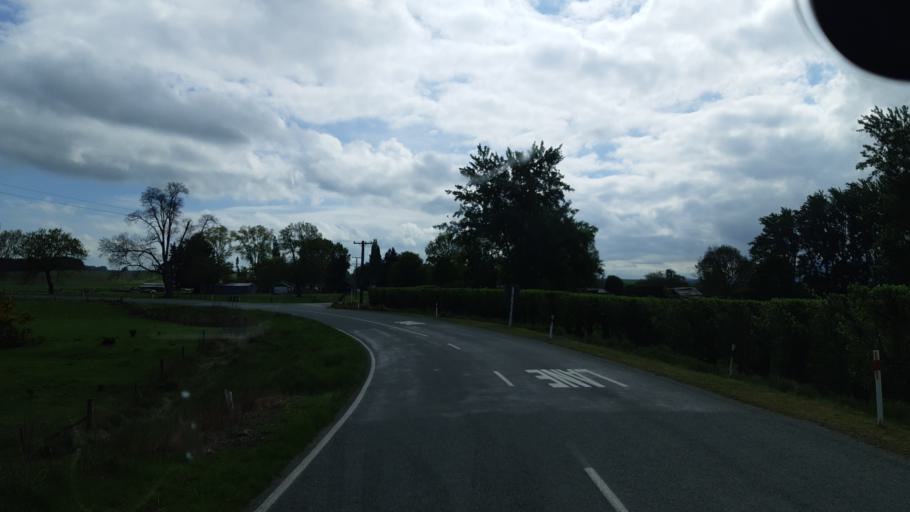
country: NZ
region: Canterbury
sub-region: Timaru District
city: Pleasant Point
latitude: -44.1718
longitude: 171.2123
